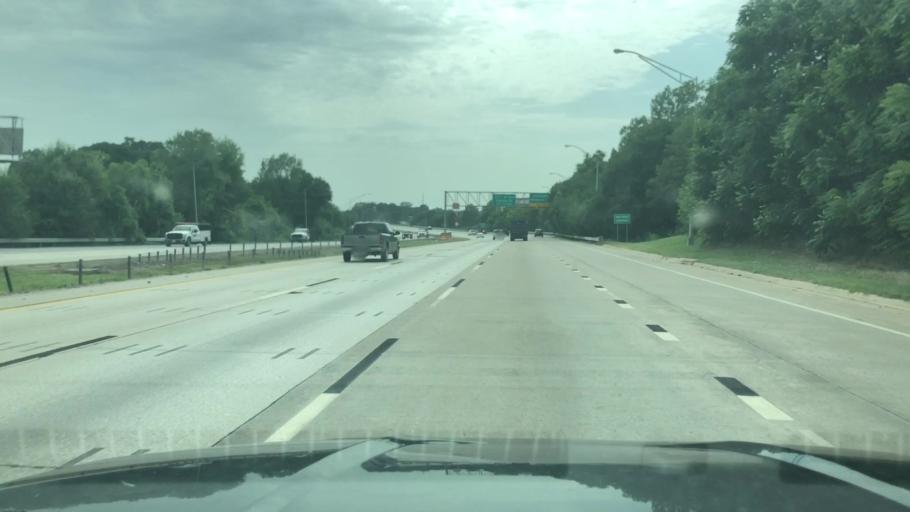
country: US
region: Oklahoma
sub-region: Tulsa County
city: Tulsa
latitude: 36.1564
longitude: -96.0143
